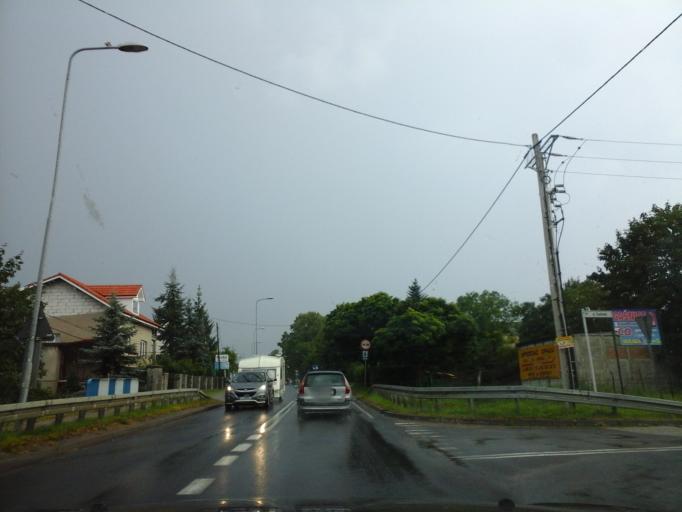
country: PL
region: Greater Poland Voivodeship
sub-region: Powiat miedzychodzki
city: Miedzychod
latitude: 52.5946
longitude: 15.8946
